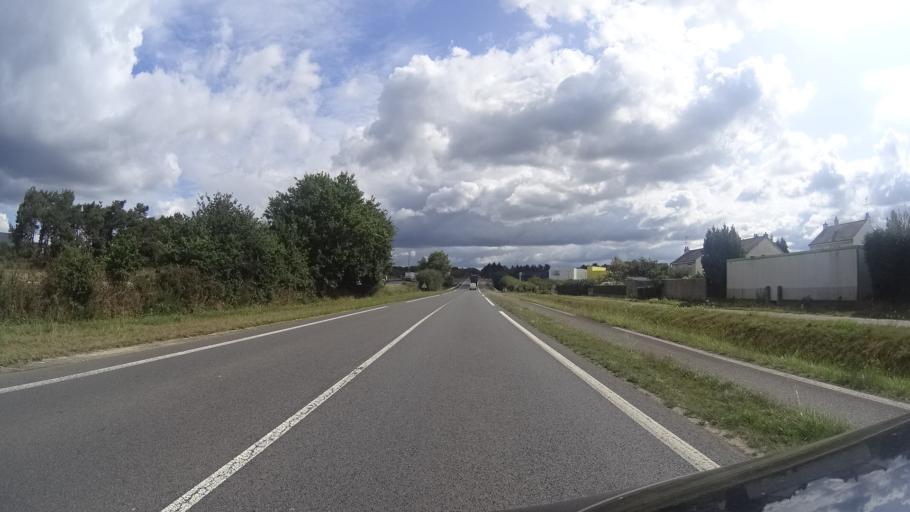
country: FR
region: Pays de la Loire
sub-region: Departement de la Loire-Atlantique
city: Savenay
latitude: 47.3650
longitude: -1.9466
